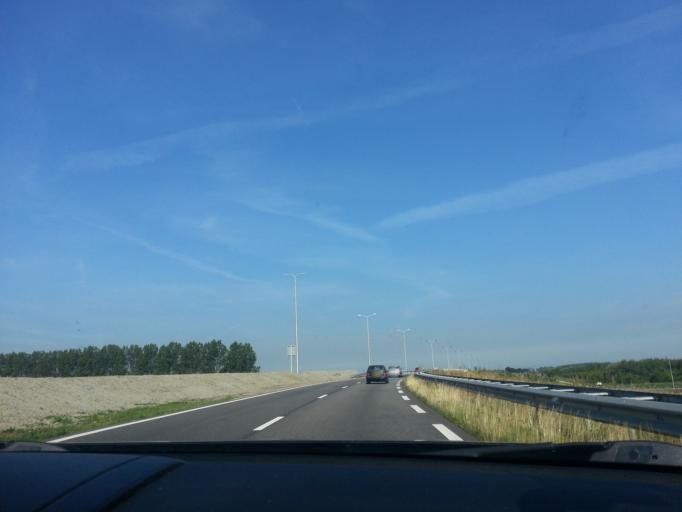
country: NL
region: South Holland
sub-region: Gemeente Kaag en Braassem
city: Oude Wetering
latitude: 52.2520
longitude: 4.6194
